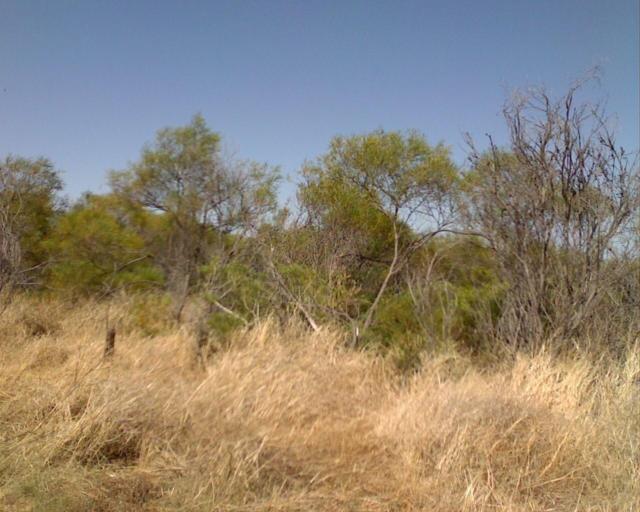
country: AU
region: Western Australia
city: Port Denison
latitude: -29.6601
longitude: 115.2279
